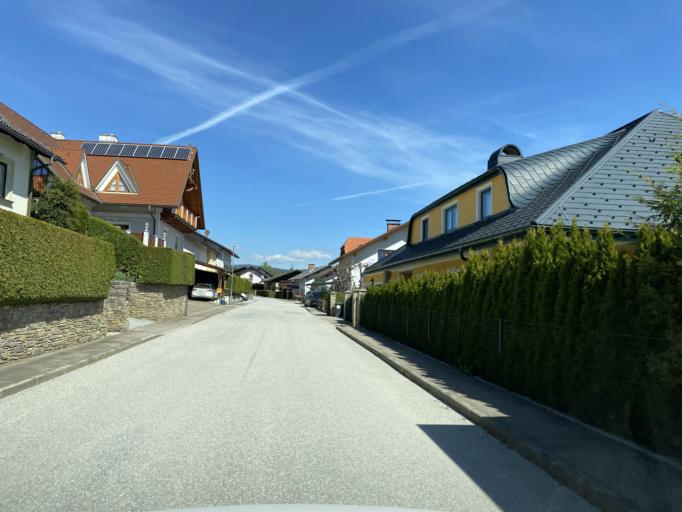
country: AT
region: Styria
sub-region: Politischer Bezirk Weiz
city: Birkfeld
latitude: 47.3472
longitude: 15.6946
